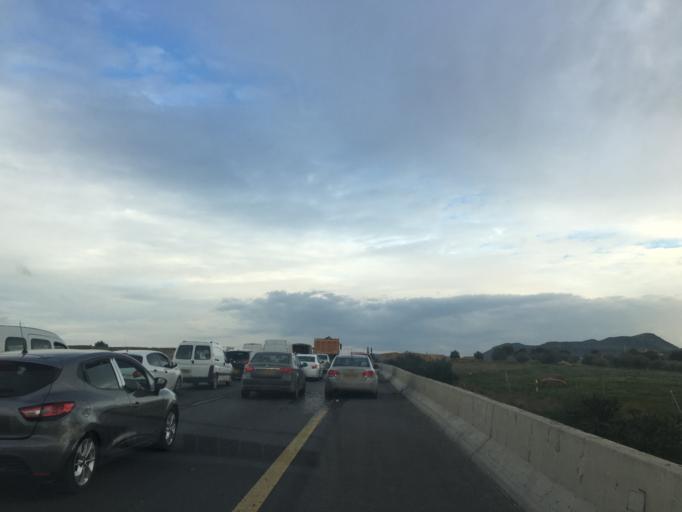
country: DZ
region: Bouira
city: Chorfa
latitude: 36.3184
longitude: 4.1431
